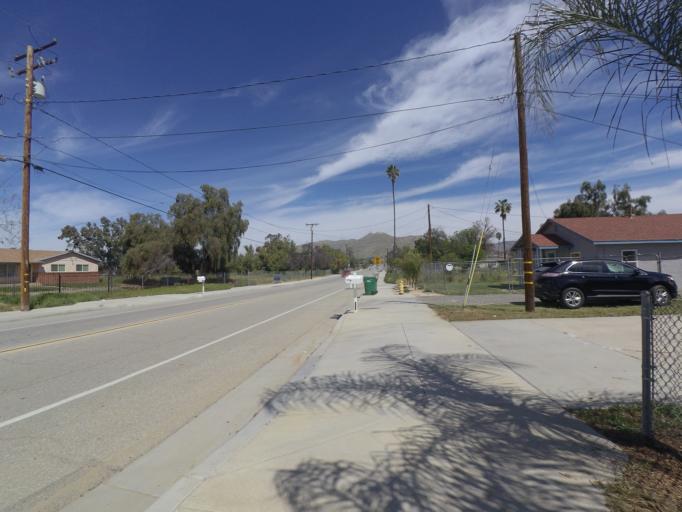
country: US
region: California
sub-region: Riverside County
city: March Air Force Base
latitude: 33.9222
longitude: -117.2787
